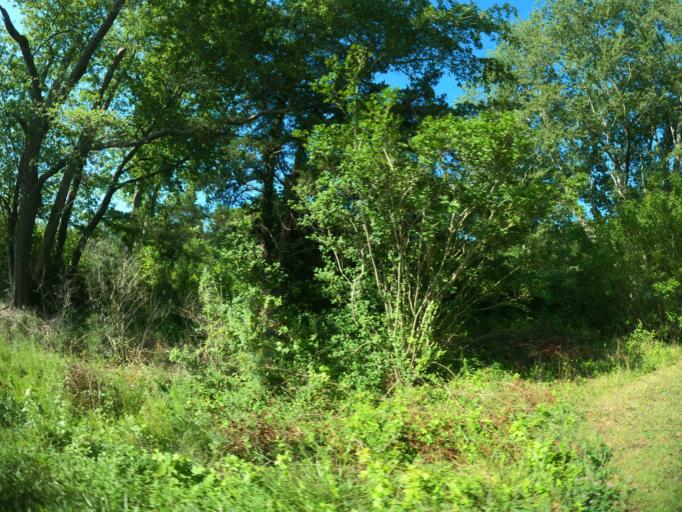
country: US
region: Delaware
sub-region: Sussex County
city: Ocean View
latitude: 38.4925
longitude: -75.1272
